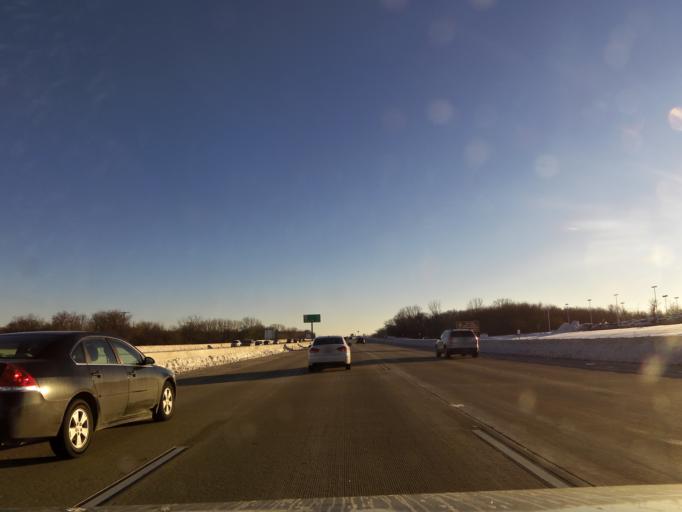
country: US
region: Wisconsin
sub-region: Kenosha County
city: Pleasant Prairie
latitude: 42.5573
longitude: -87.9527
